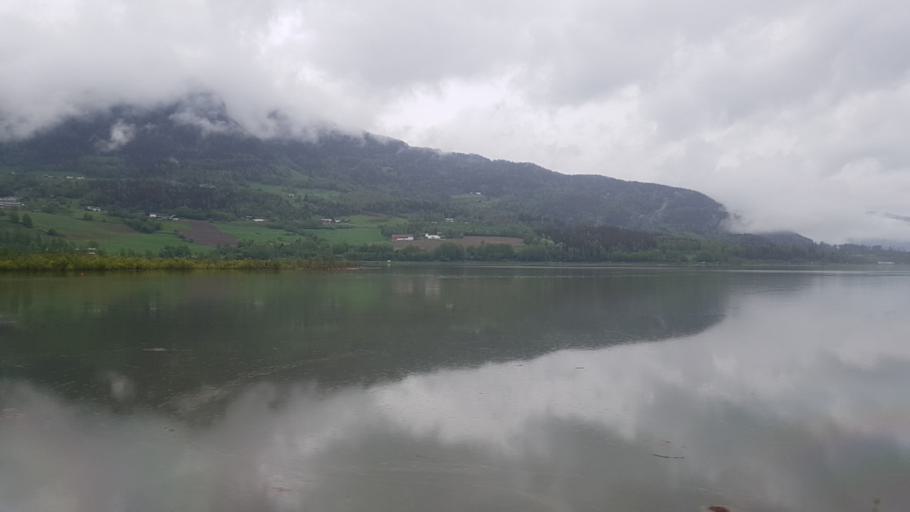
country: NO
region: Oppland
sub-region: Oyer
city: Tretten
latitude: 61.4236
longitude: 10.2281
